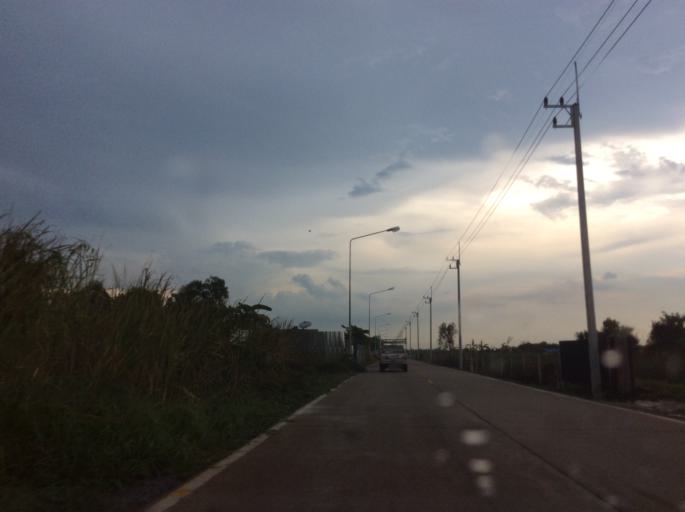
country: TH
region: Pathum Thani
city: Thanyaburi
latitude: 14.0031
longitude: 100.7502
